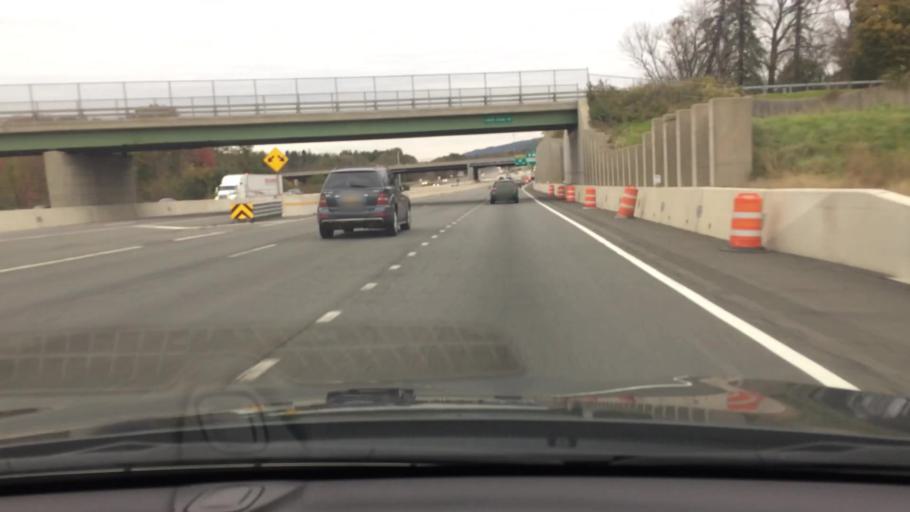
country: US
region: New York
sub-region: Orange County
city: Harriman
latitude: 41.3047
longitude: -74.1305
